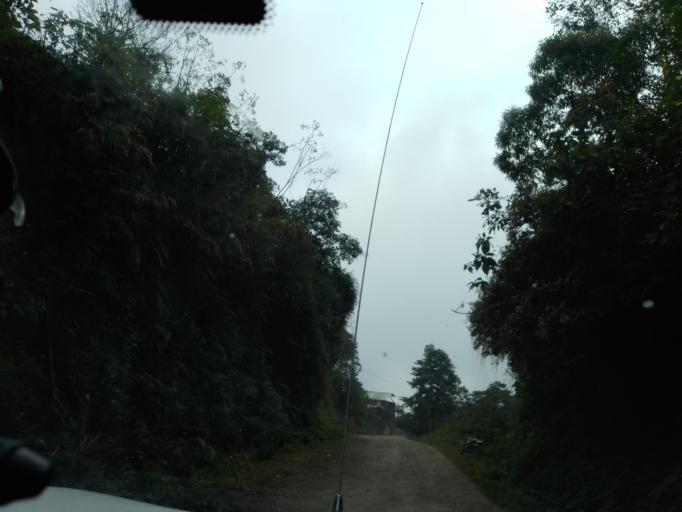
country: MX
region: Chiapas
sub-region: Union Juarez
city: Santo Domingo
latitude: 15.0948
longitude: -92.1011
